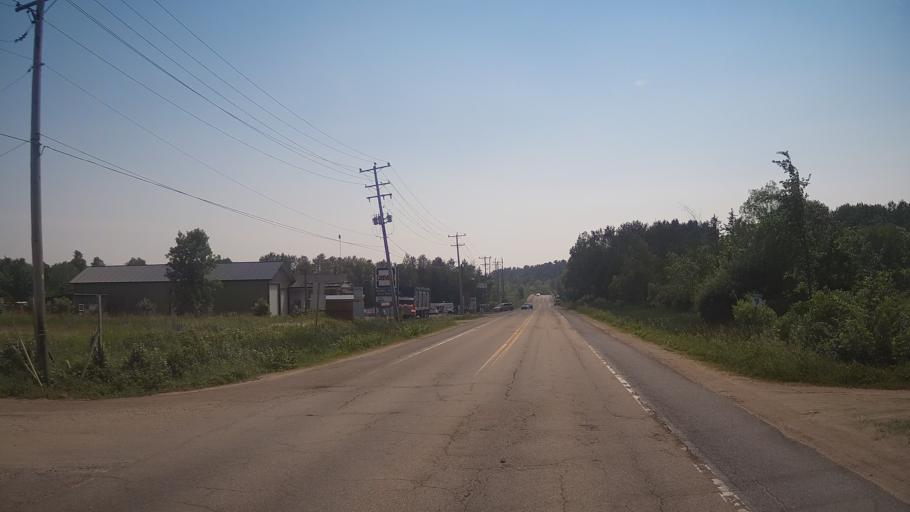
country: CA
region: Ontario
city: Pembroke
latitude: 45.8191
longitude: -77.0236
